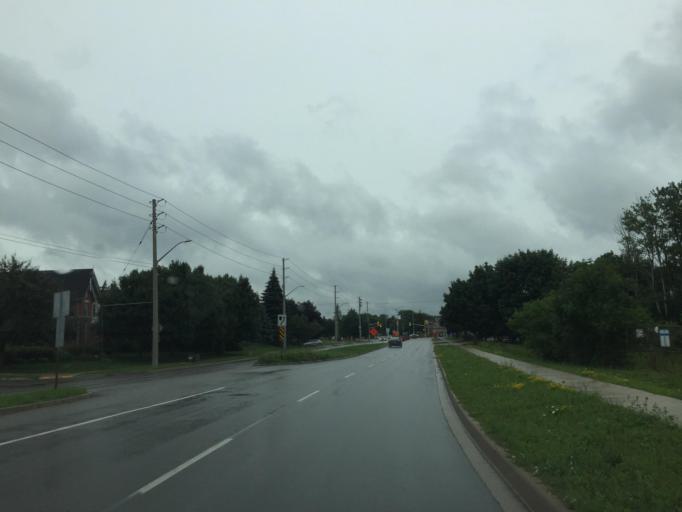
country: CA
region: Ontario
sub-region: Wellington County
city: Guelph
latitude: 43.5205
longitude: -80.2144
